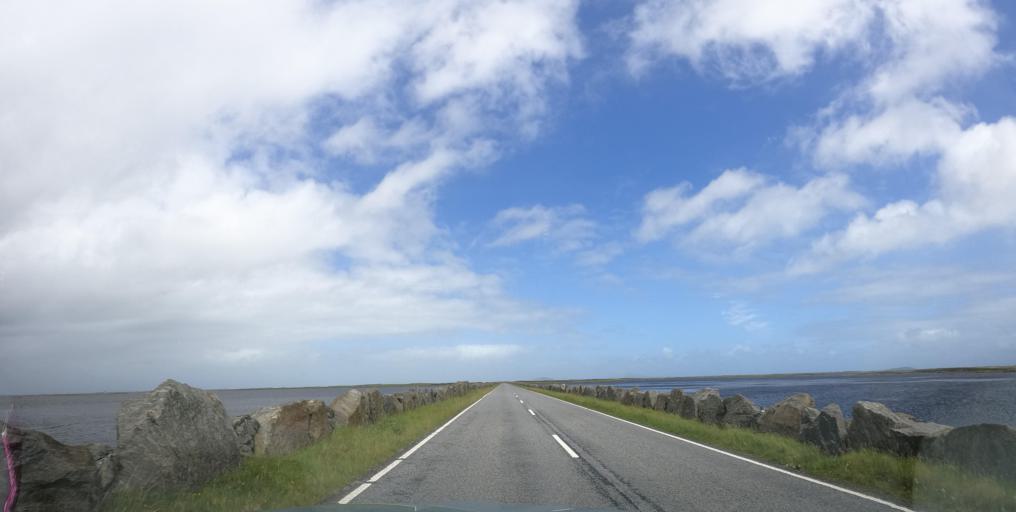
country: GB
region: Scotland
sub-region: Eilean Siar
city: Benbecula
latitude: 57.3583
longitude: -7.3566
